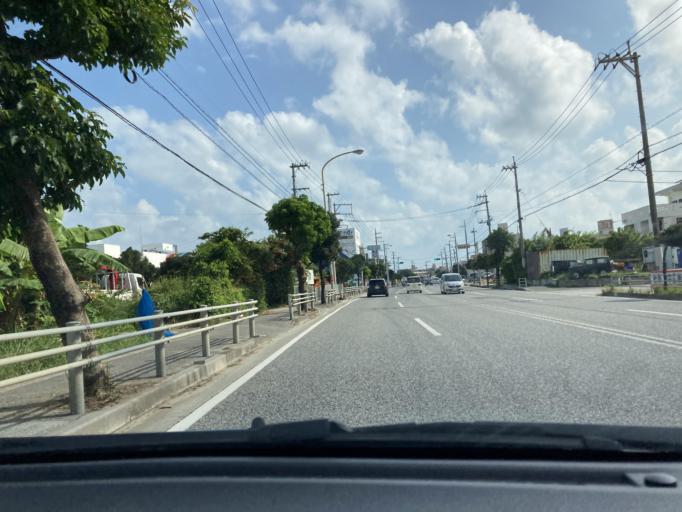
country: JP
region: Okinawa
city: Chatan
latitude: 26.2865
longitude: 127.8149
